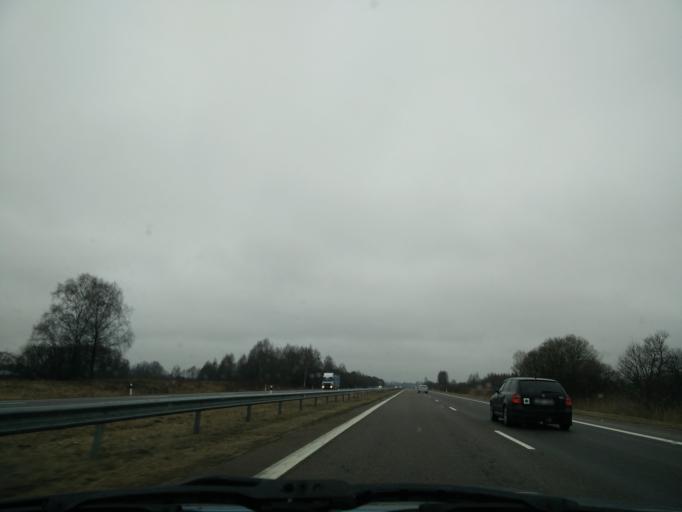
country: LT
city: Skaudvile
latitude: 55.4332
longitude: 22.7448
